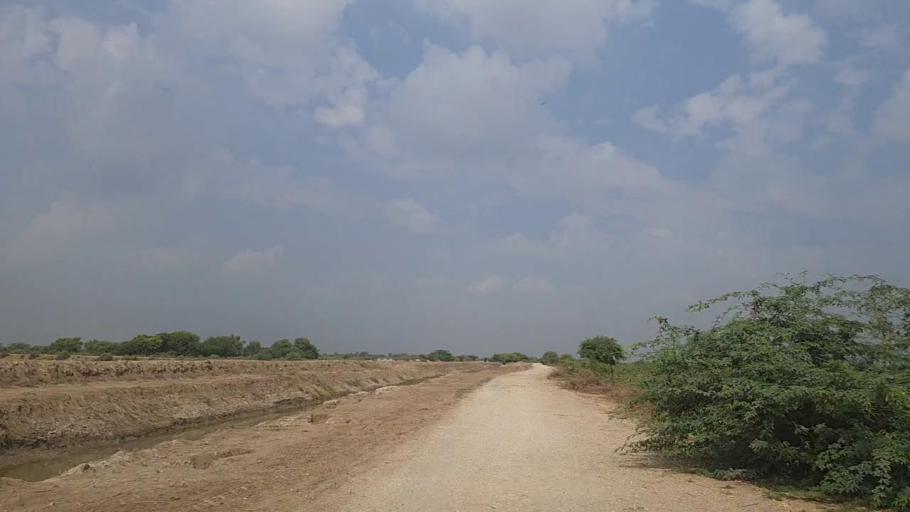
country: PK
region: Sindh
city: Daro Mehar
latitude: 24.6957
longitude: 68.1268
